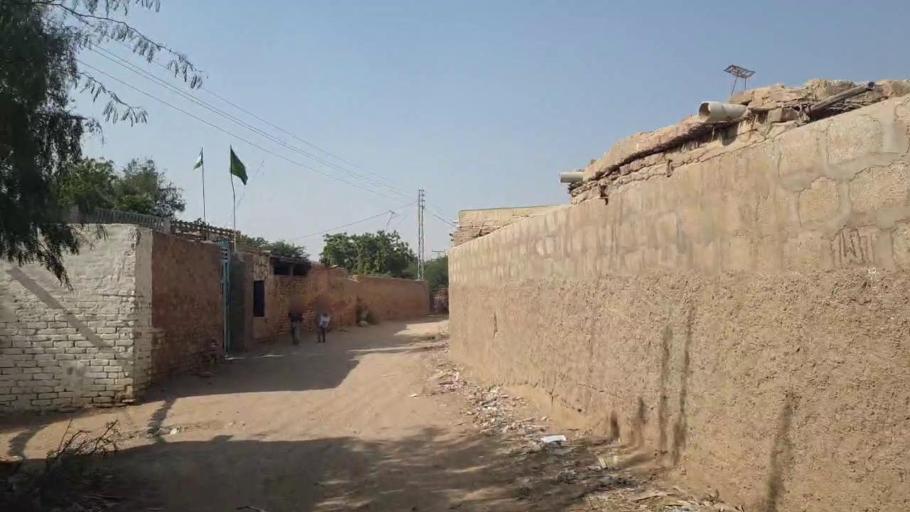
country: PK
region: Sindh
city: Kotri
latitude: 25.3204
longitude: 68.2386
